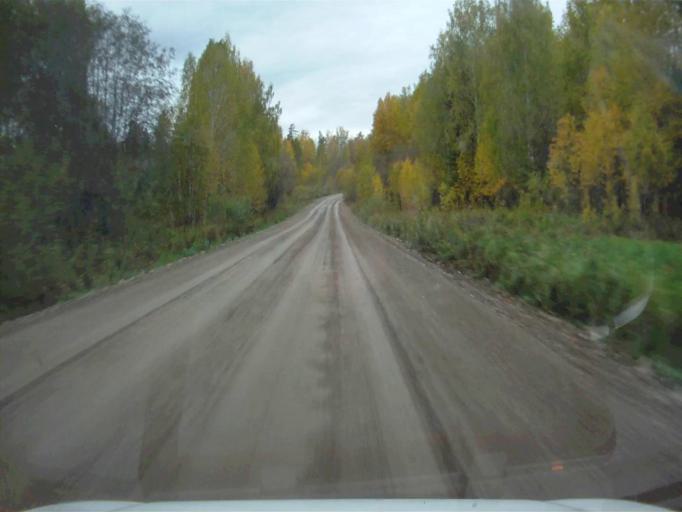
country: RU
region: Chelyabinsk
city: Nyazepetrovsk
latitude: 56.1091
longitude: 59.3763
